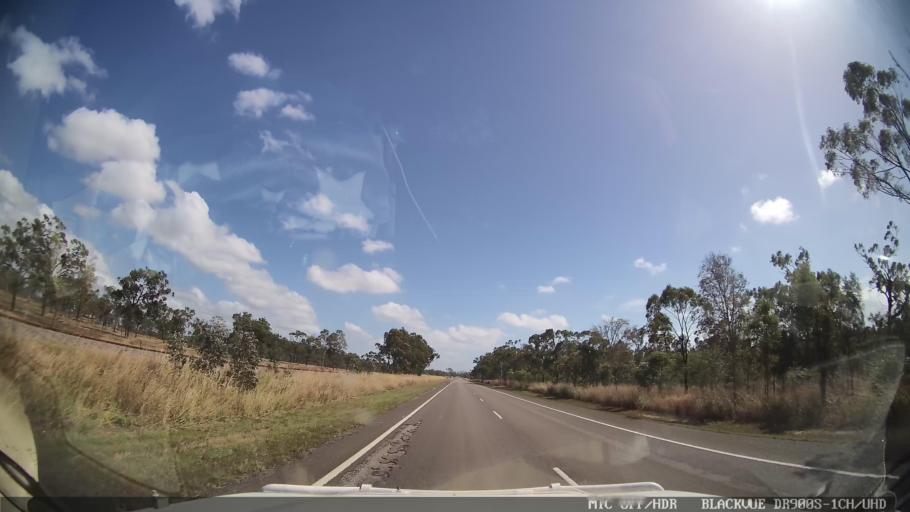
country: AU
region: Queensland
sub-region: Whitsunday
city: Red Hill
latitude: -20.1860
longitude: 148.3562
